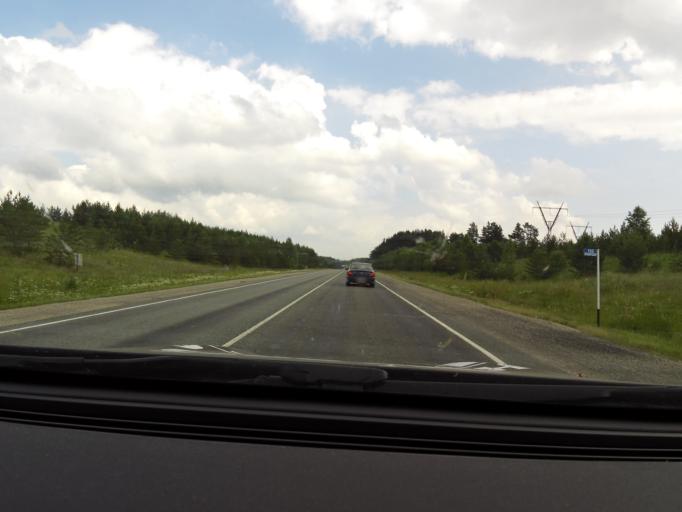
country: RU
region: Sverdlovsk
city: Achit
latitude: 56.7813
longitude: 57.9230
